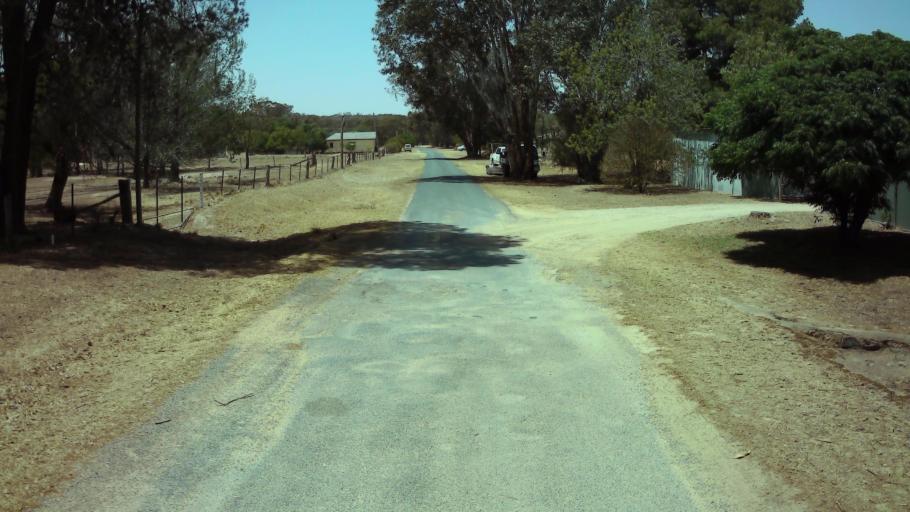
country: AU
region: New South Wales
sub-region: Weddin
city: Grenfell
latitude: -33.8899
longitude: 148.1696
